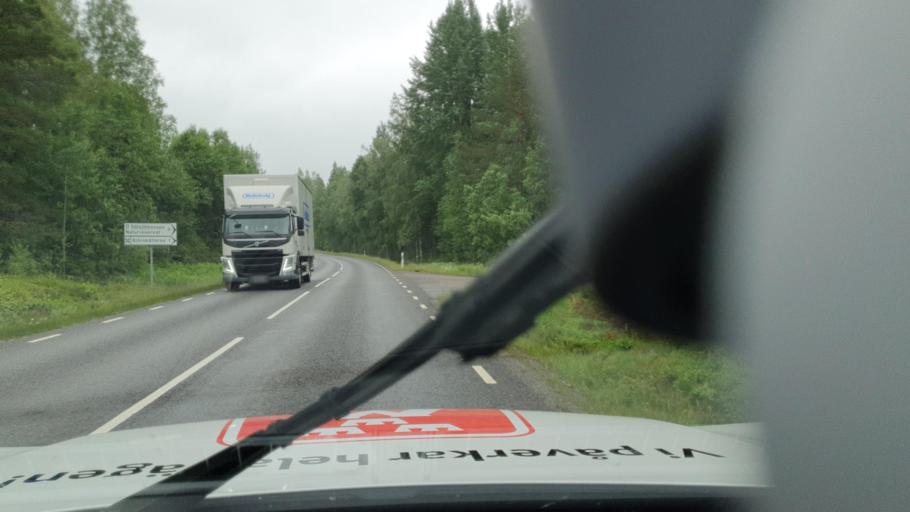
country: SE
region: Vaermland
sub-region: Kristinehamns Kommun
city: Bjorneborg
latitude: 59.2223
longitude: 14.3121
